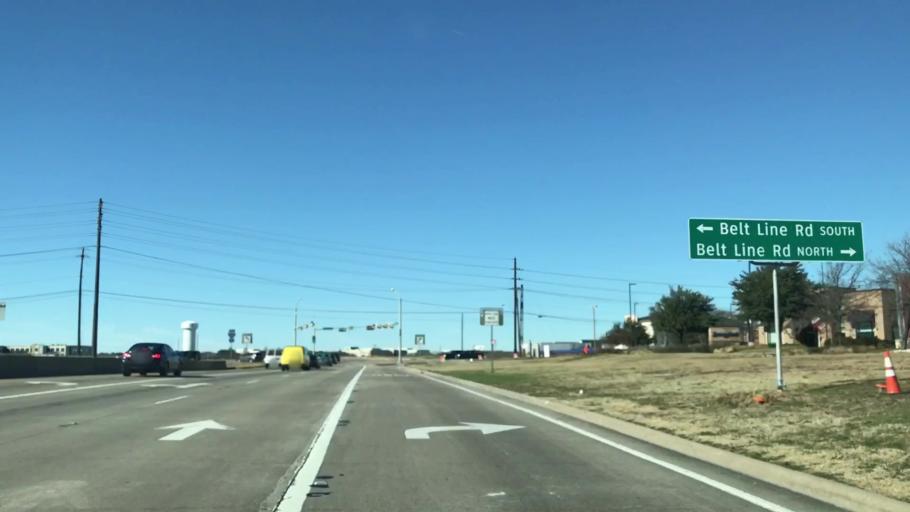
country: US
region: Texas
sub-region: Dallas County
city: Coppell
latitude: 32.9241
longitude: -96.9922
